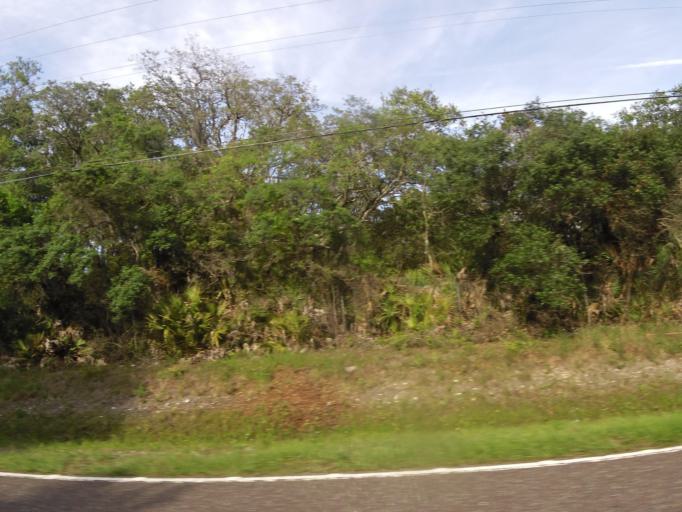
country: US
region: Florida
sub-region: Duval County
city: Atlantic Beach
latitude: 30.4739
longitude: -81.4697
